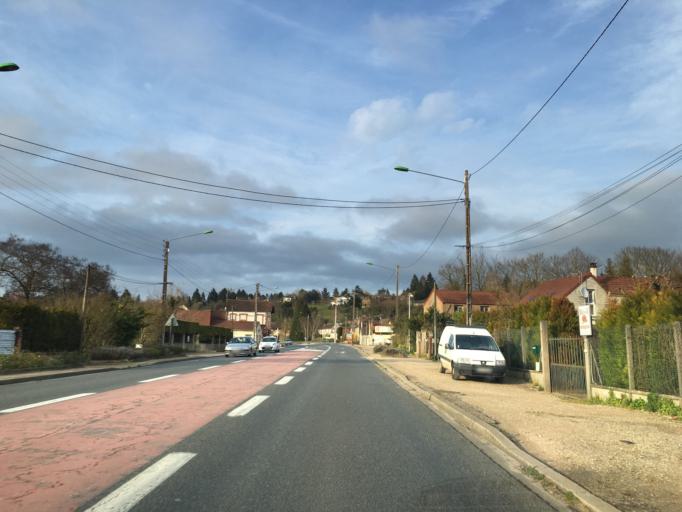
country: FR
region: Bourgogne
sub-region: Departement de l'Yonne
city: Veron
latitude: 48.1492
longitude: 3.3086
